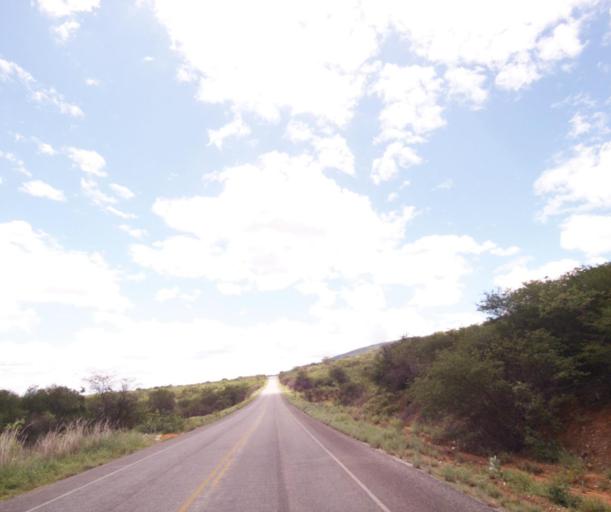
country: BR
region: Bahia
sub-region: Brumado
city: Brumado
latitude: -14.2365
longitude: -41.6945
